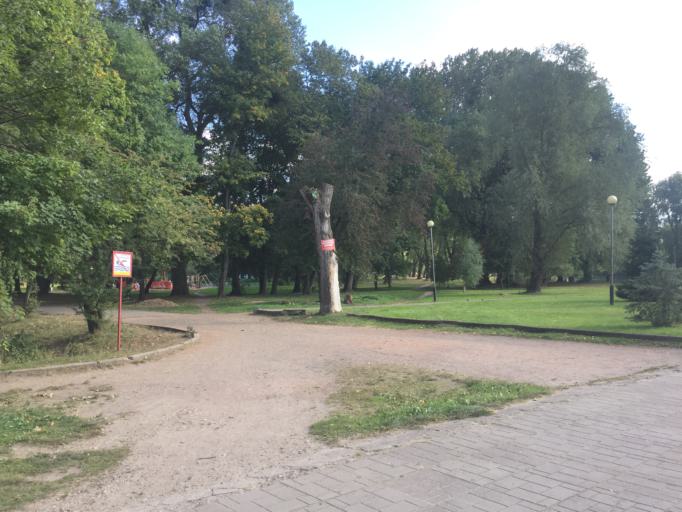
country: RU
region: Kaliningrad
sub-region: Gorod Kaliningrad
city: Kaliningrad
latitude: 54.6939
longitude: 20.5099
